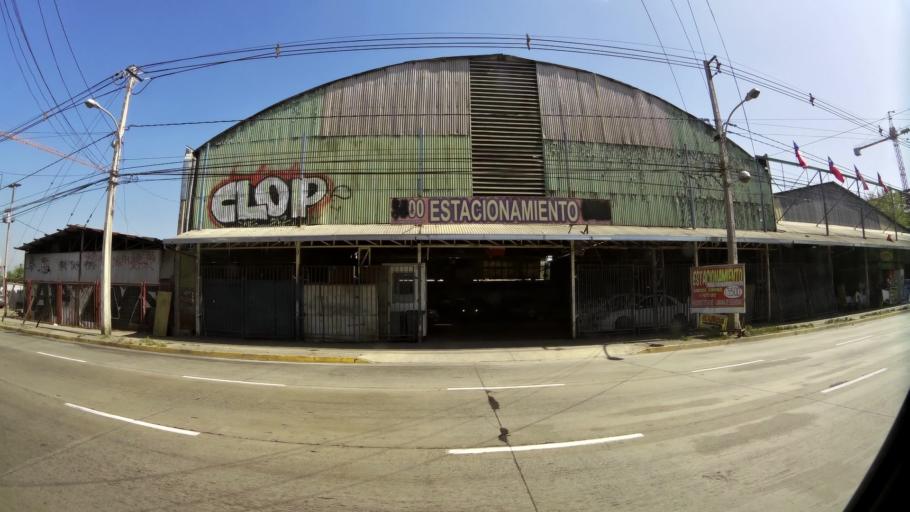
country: CL
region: Santiago Metropolitan
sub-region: Provincia de Santiago
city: Santiago
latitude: -33.4758
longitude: -70.6421
